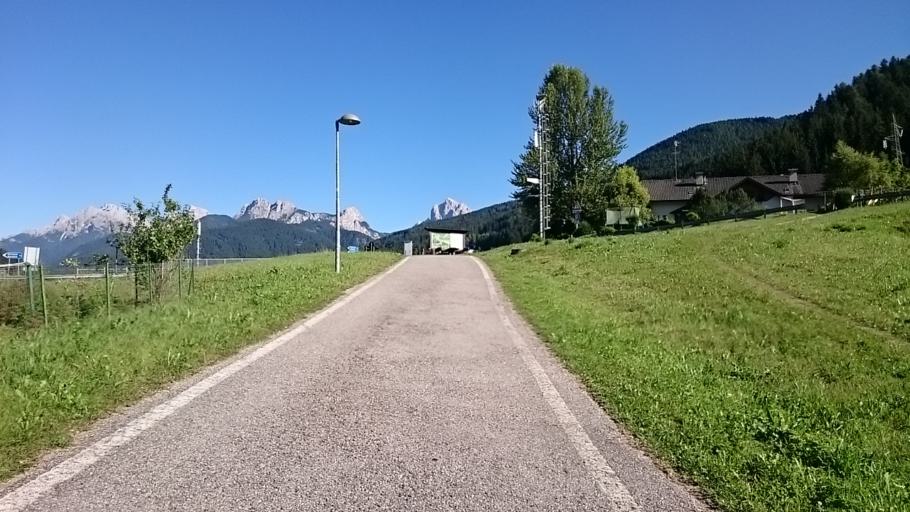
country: IT
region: Trentino-Alto Adige
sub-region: Bolzano
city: Monguelfo
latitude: 46.7531
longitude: 12.1050
